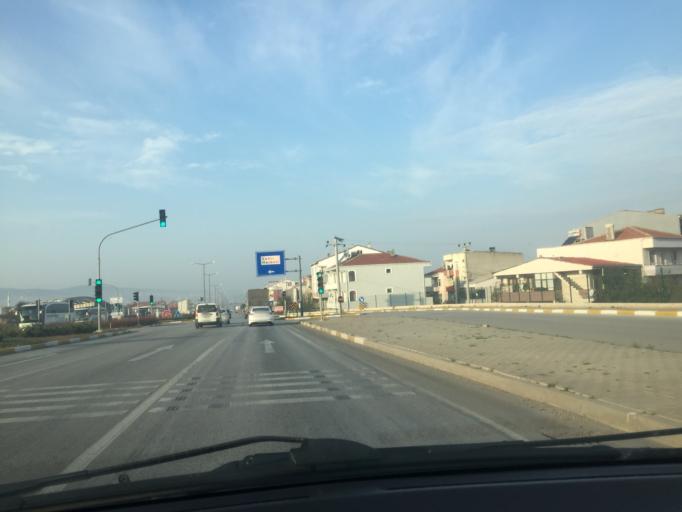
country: TR
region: Canakkale
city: Biga
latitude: 40.2445
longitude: 27.2746
